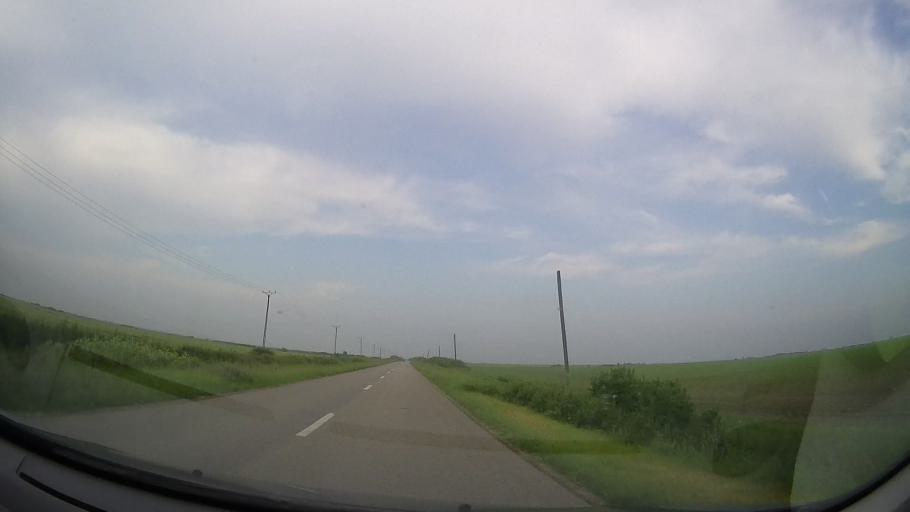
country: RO
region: Timis
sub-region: Comuna Foeni
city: Foeni
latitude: 45.5232
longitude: 20.9185
